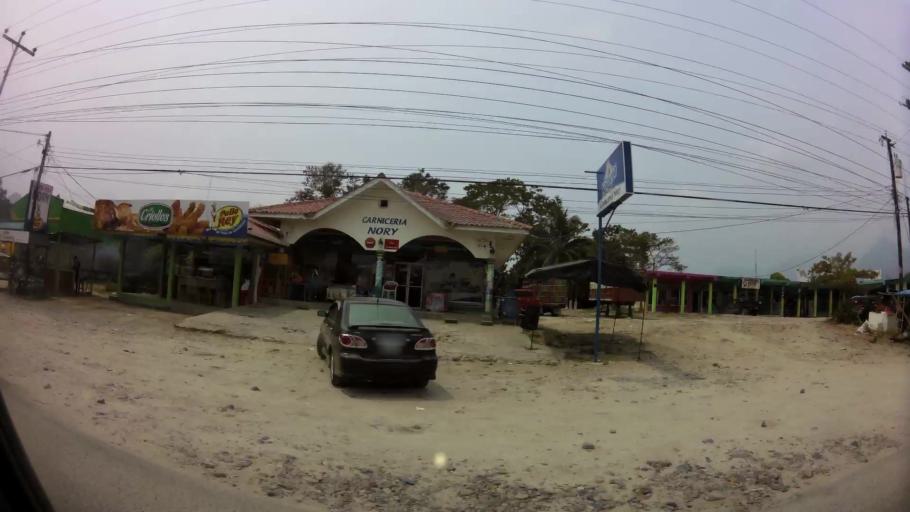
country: HN
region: Atlantida
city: San Juan Pueblo
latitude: 15.5989
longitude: -87.2103
